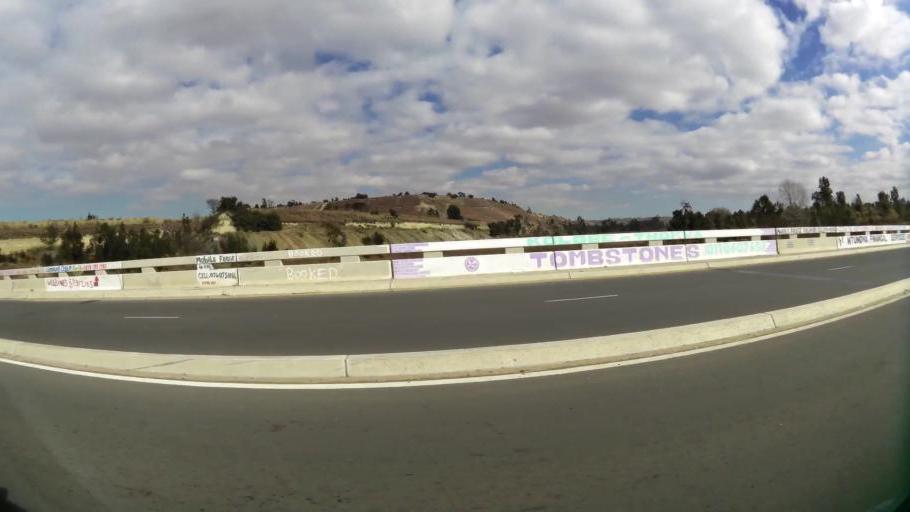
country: ZA
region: Gauteng
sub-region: City of Johannesburg Metropolitan Municipality
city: Roodepoort
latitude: -26.1955
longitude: 27.9023
